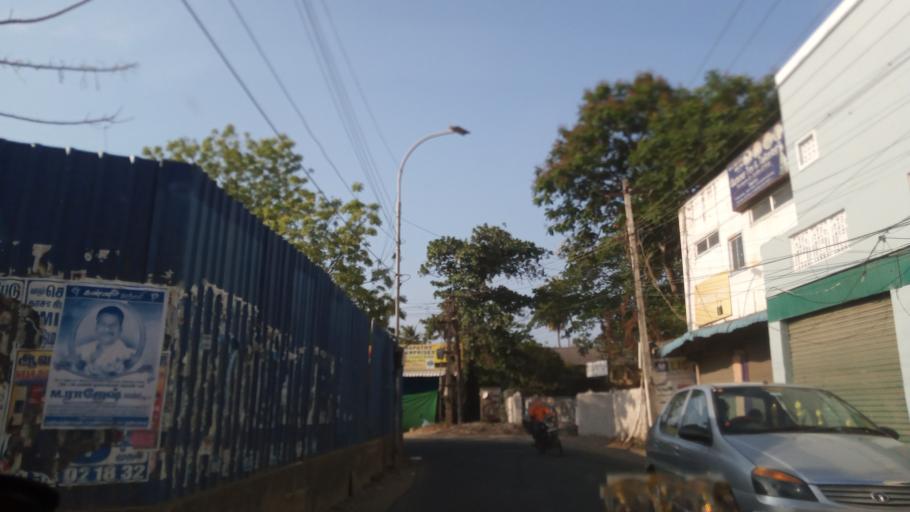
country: IN
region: Tamil Nadu
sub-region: Kancheepuram
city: Manappakkam
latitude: 13.0235
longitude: 80.1840
